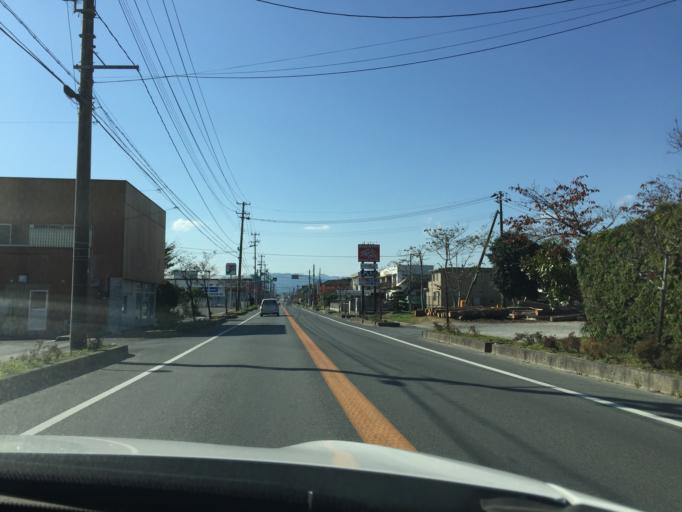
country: JP
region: Miyagi
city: Marumori
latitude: 37.8066
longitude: 140.9340
